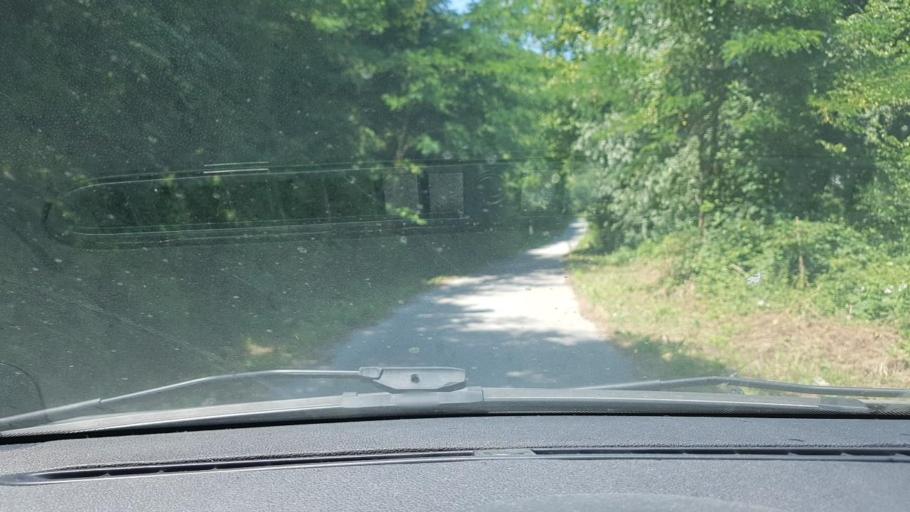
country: BA
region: Federation of Bosnia and Herzegovina
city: Orasac
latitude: 44.5614
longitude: 16.0833
